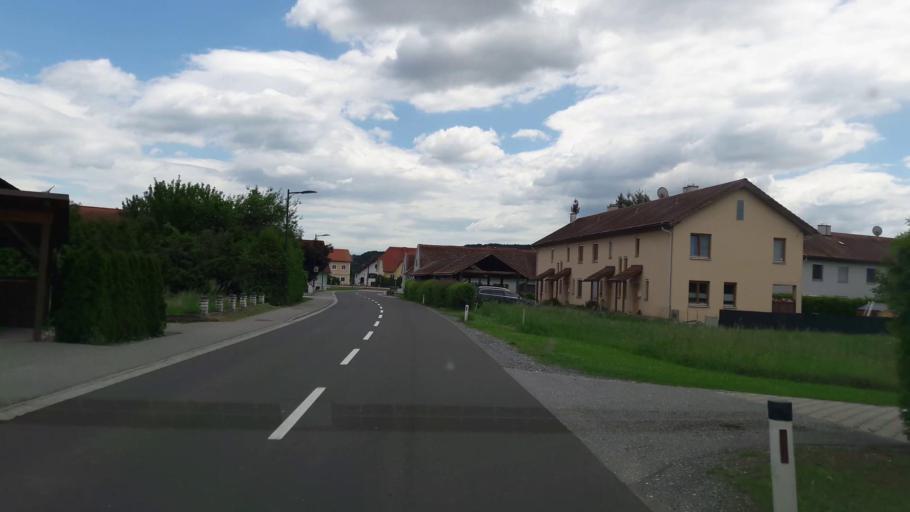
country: AT
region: Styria
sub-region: Politischer Bezirk Hartberg-Fuerstenfeld
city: UEbersbach
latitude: 47.0212
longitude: 16.0508
